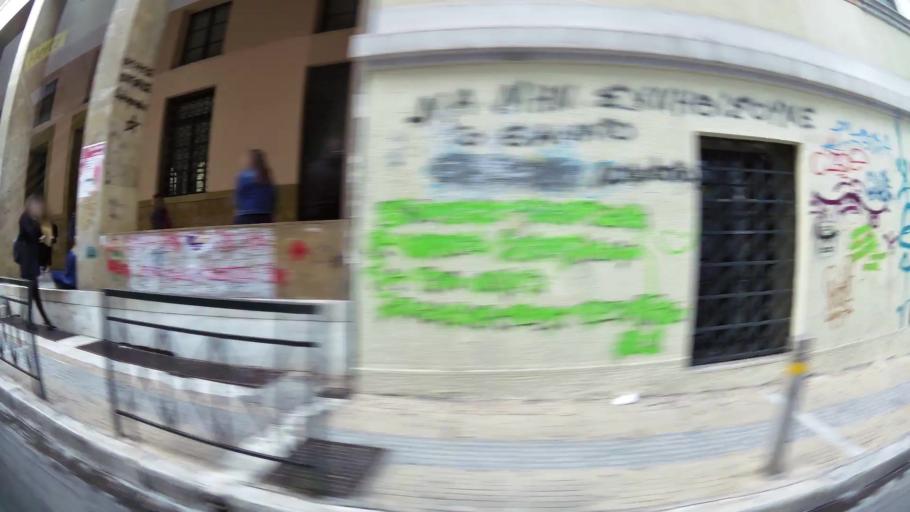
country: GR
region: Attica
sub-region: Nomarchia Athinas
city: Athens
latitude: 37.9812
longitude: 23.7360
